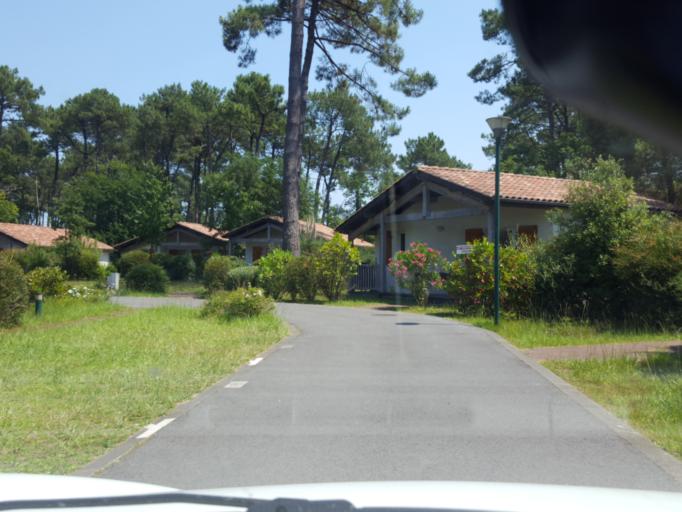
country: FR
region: Aquitaine
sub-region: Departement des Landes
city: Ondres
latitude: 43.5721
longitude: -1.4675
